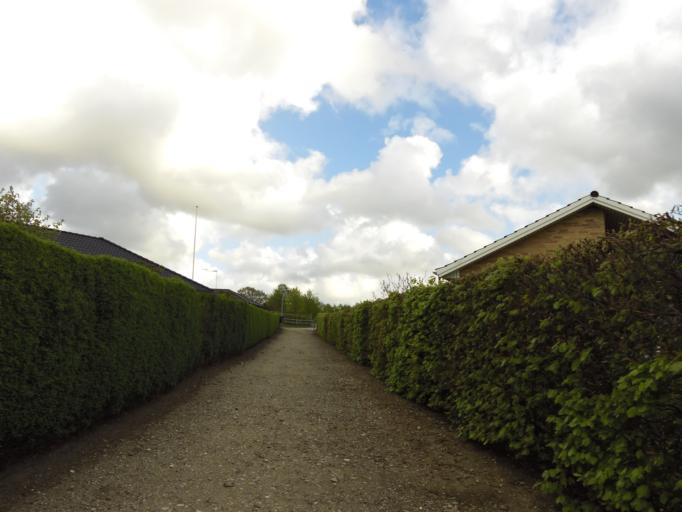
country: DK
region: South Denmark
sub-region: Haderslev Kommune
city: Gram
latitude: 55.2949
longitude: 9.0413
